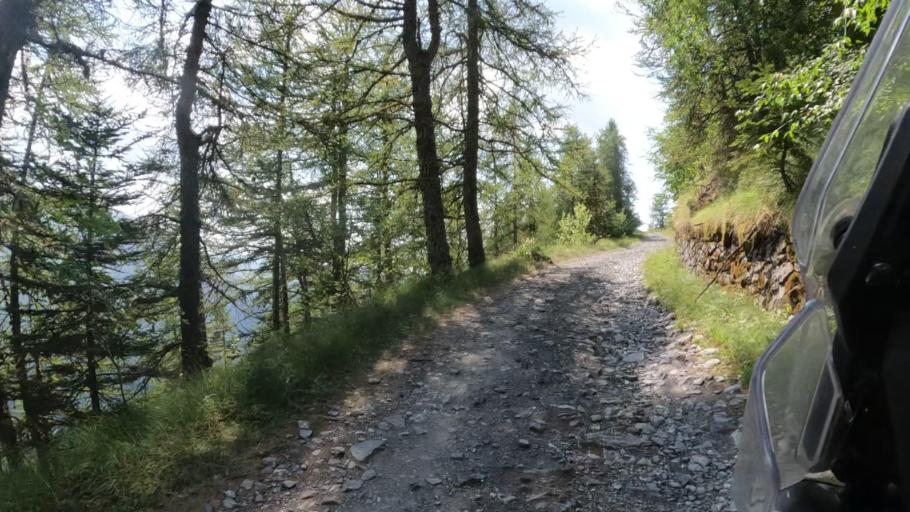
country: IT
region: Piedmont
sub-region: Provincia di Cuneo
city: Briga Alta
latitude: 44.0441
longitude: 7.7047
